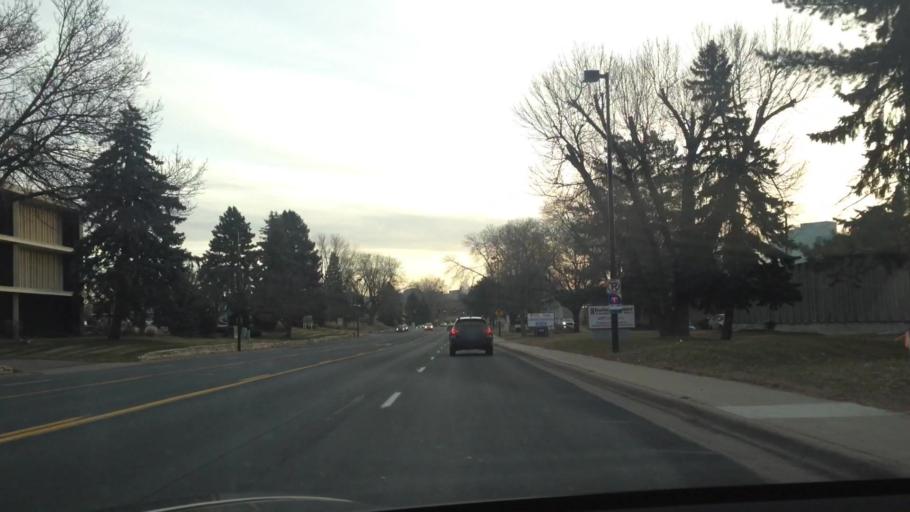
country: US
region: Minnesota
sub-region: Hennepin County
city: Edina
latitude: 44.8631
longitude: -93.3403
